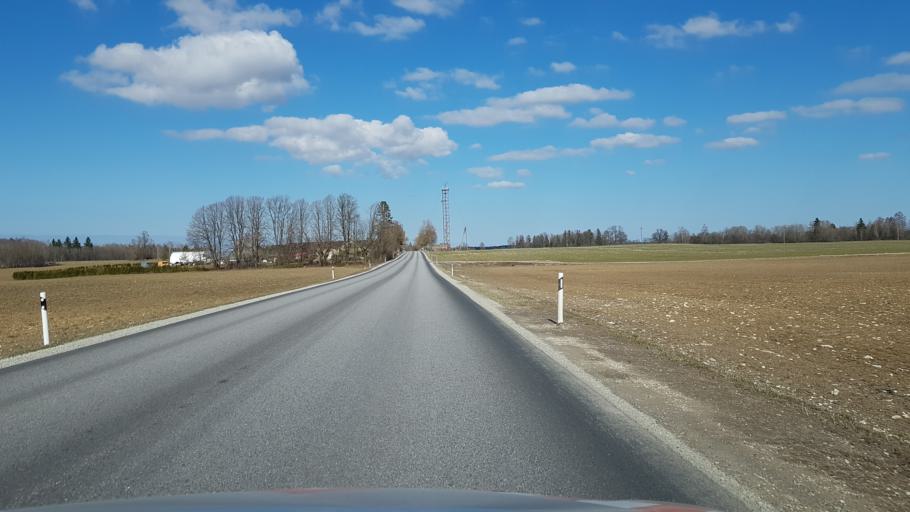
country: EE
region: Laeaene-Virumaa
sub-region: Rakvere linn
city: Rakvere
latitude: 59.2830
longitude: 26.2976
